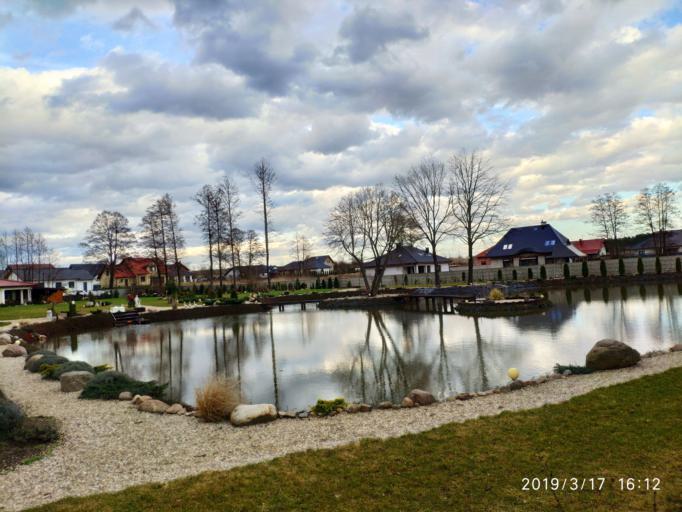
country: PL
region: Lubusz
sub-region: Powiat zielonogorski
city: Zabor
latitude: 51.9303
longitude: 15.6251
